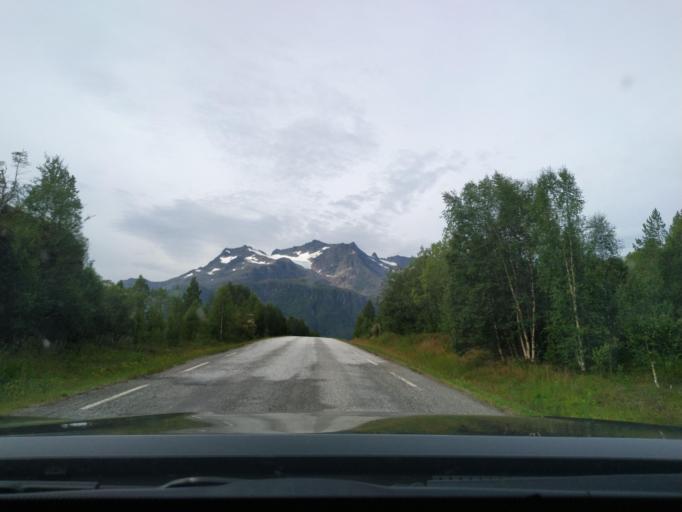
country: NO
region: Troms
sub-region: Dyroy
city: Brostadbotn
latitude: 68.9063
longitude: 17.4991
